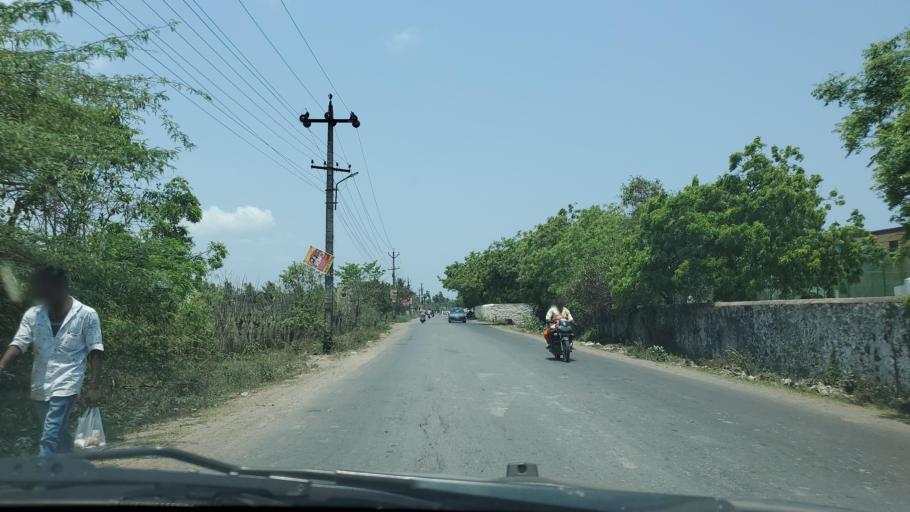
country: IN
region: Tamil Nadu
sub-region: Kancheepuram
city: Vengavasal
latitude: 12.8500
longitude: 80.1707
